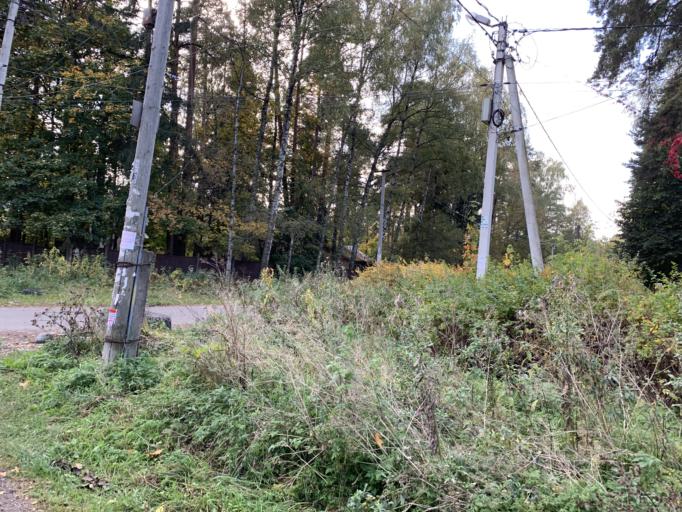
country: RU
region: Moskovskaya
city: Mamontovka
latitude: 55.9813
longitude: 37.8314
